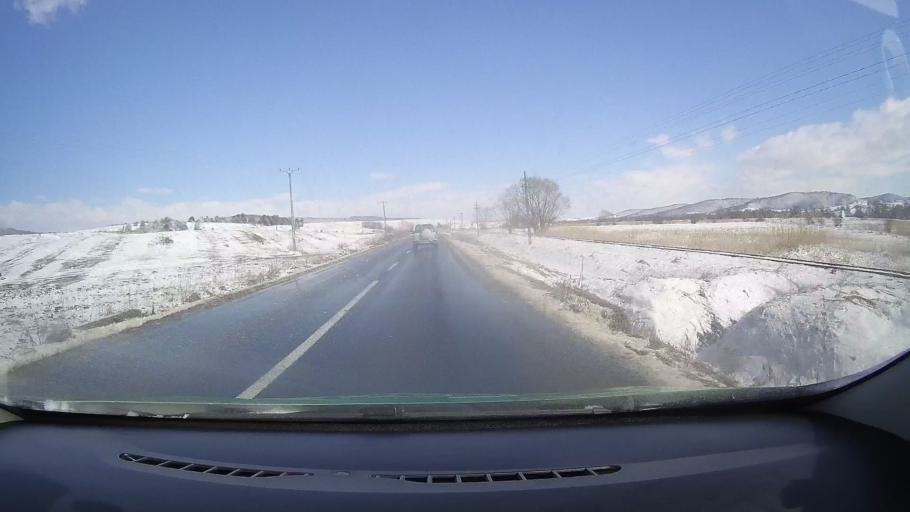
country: RO
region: Sibiu
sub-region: Comuna Rosia
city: Rosia
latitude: 45.8082
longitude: 24.3585
